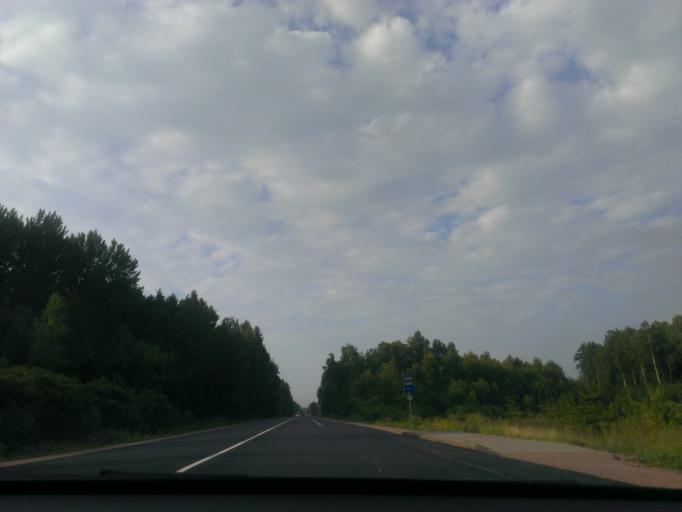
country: LV
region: Lecava
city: Iecava
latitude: 56.6942
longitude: 24.2420
